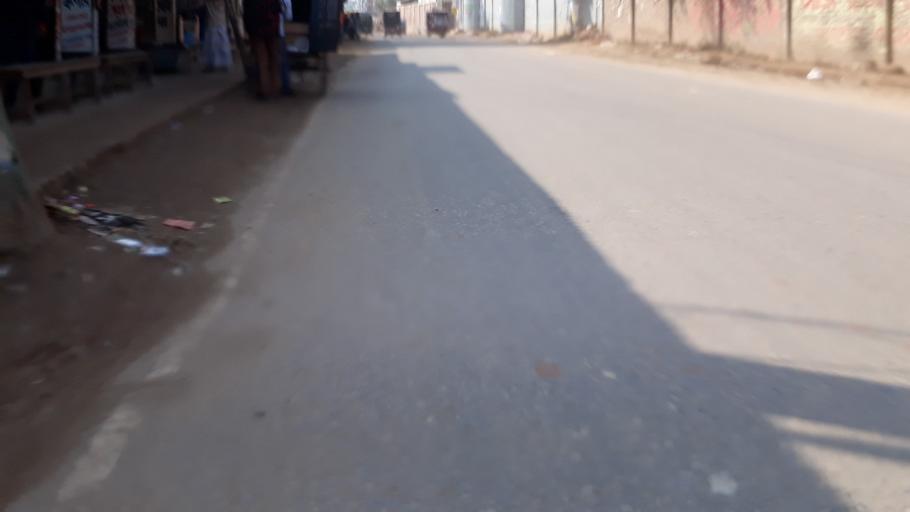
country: BD
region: Dhaka
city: Tungi
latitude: 23.9076
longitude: 90.2900
